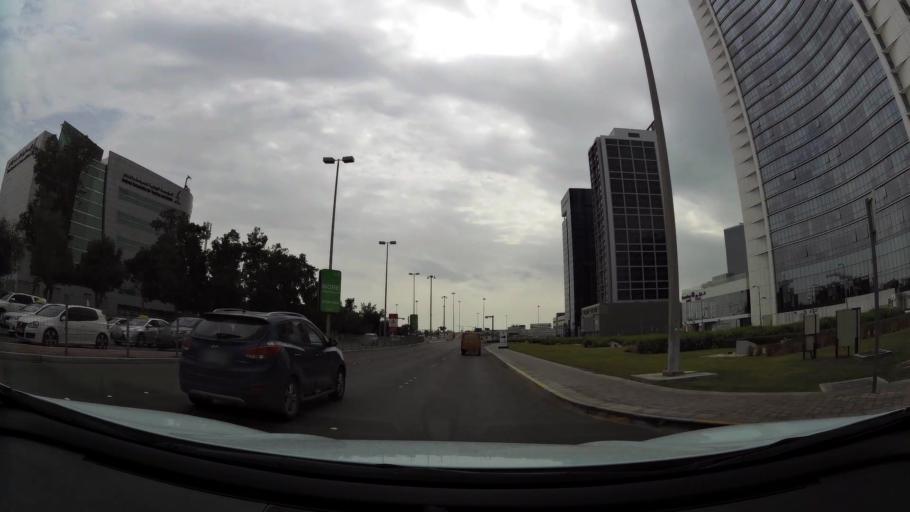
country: AE
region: Abu Dhabi
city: Abu Dhabi
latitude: 24.4207
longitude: 54.4441
